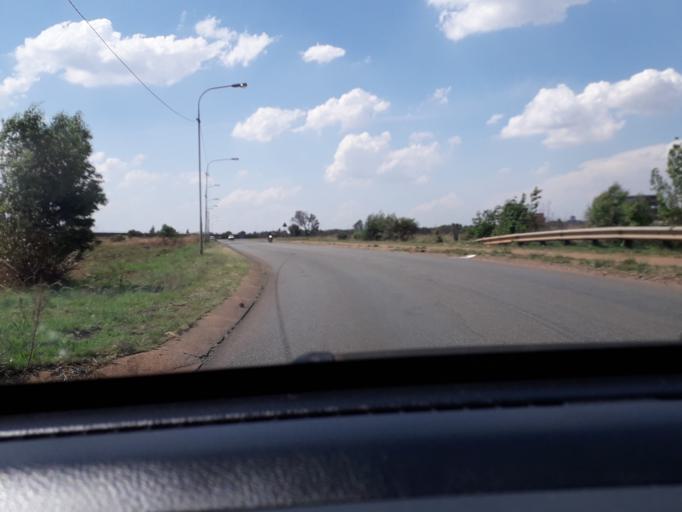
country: ZA
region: Gauteng
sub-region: City of Tshwane Metropolitan Municipality
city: Centurion
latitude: -25.8495
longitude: 28.2265
